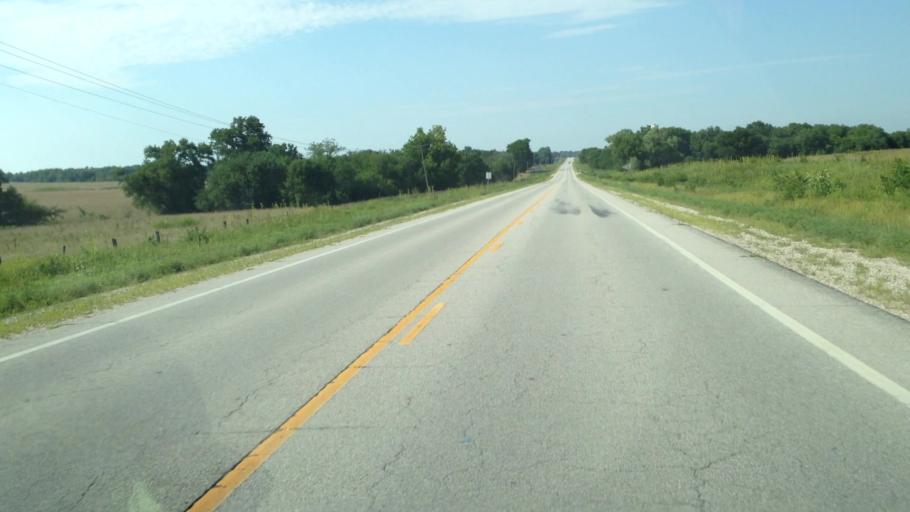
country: US
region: Kansas
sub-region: Neosho County
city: Erie
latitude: 37.5019
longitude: -95.2697
